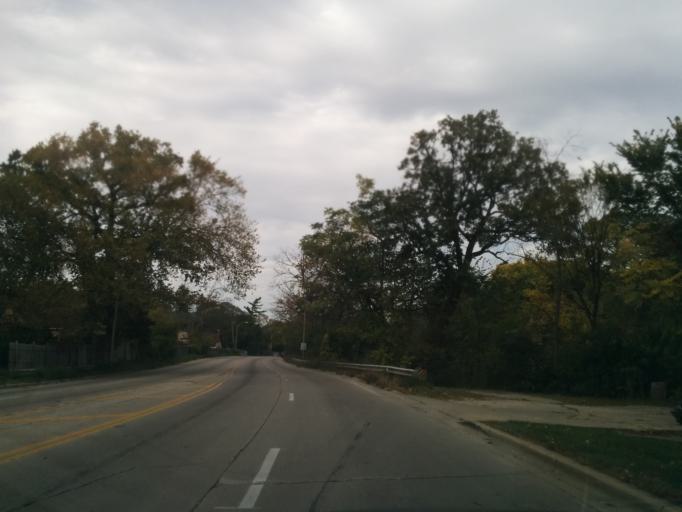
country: US
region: Illinois
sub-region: Cook County
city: Maywood
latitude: 41.8940
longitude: -87.8346
